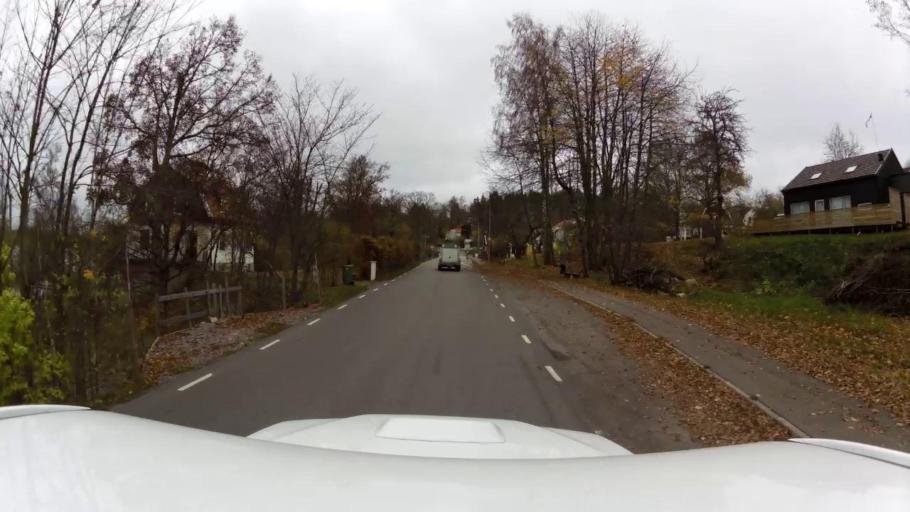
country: SE
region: OEstergoetland
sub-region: Kinda Kommun
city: Rimforsa
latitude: 58.2163
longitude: 15.6784
